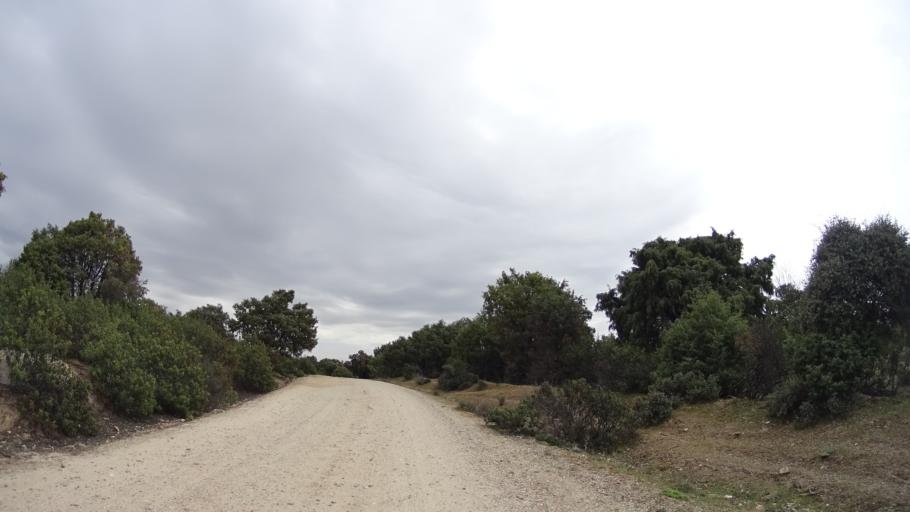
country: ES
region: Madrid
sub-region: Provincia de Madrid
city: Hoyo de Manzanares
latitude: 40.5999
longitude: -3.8851
